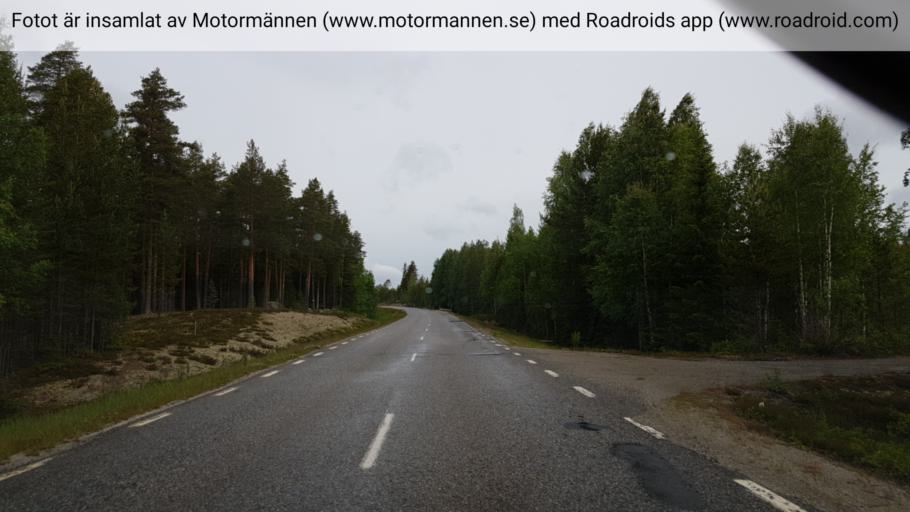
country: SE
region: Vaesterbotten
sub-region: Norsjo Kommun
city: Norsjoe
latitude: 64.6788
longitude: 19.2496
